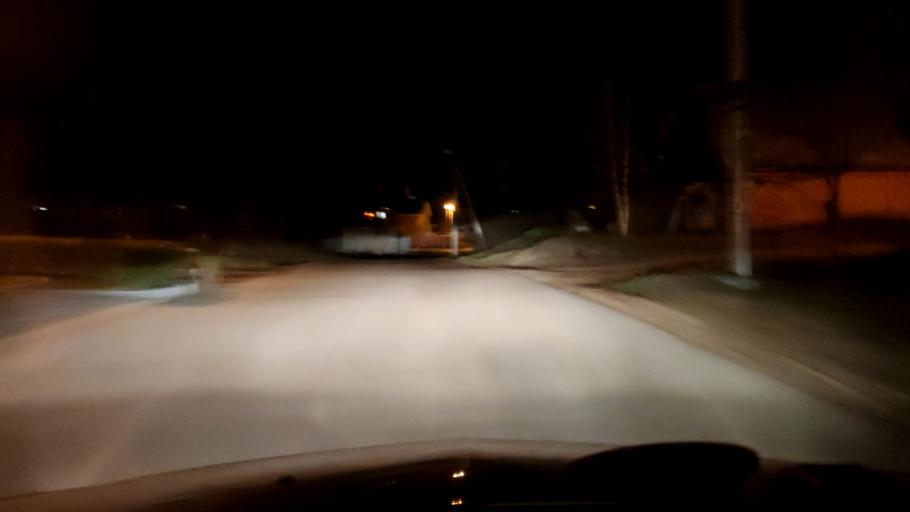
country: RU
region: Voronezj
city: Pridonskoy
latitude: 51.6424
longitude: 39.0890
